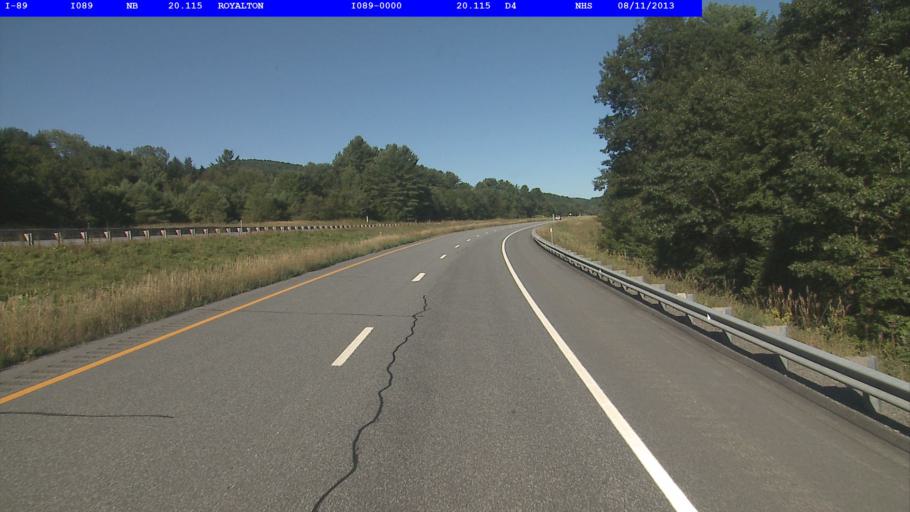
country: US
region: Vermont
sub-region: Orange County
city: Randolph
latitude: 43.8110
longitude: -72.5483
